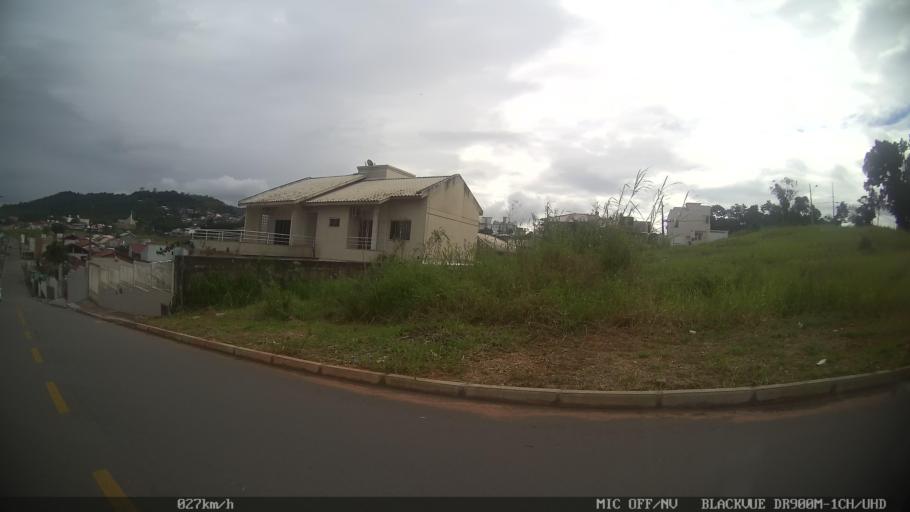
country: BR
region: Santa Catarina
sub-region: Sao Jose
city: Campinas
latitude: -27.5478
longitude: -48.6307
